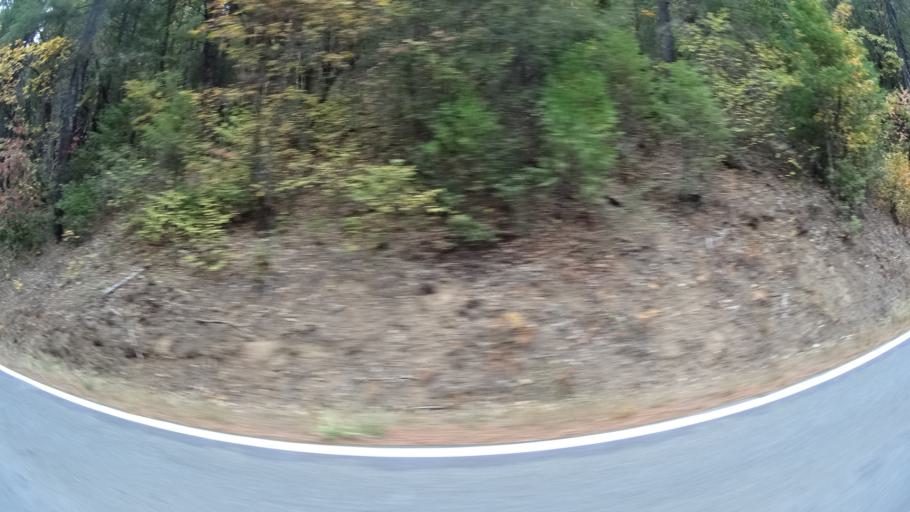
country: US
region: California
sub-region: Siskiyou County
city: Happy Camp
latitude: 41.8623
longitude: -123.4020
